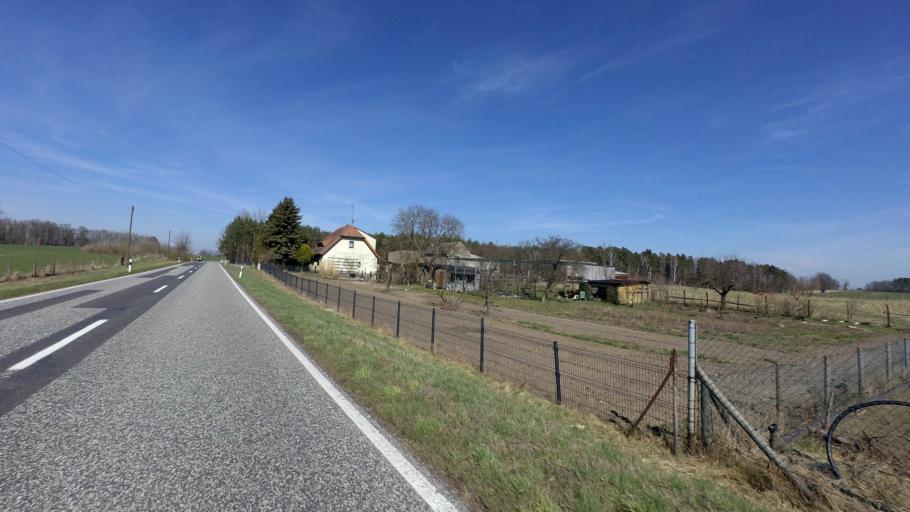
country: DE
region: Brandenburg
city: Furstenwalde
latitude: 52.4145
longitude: 14.0460
